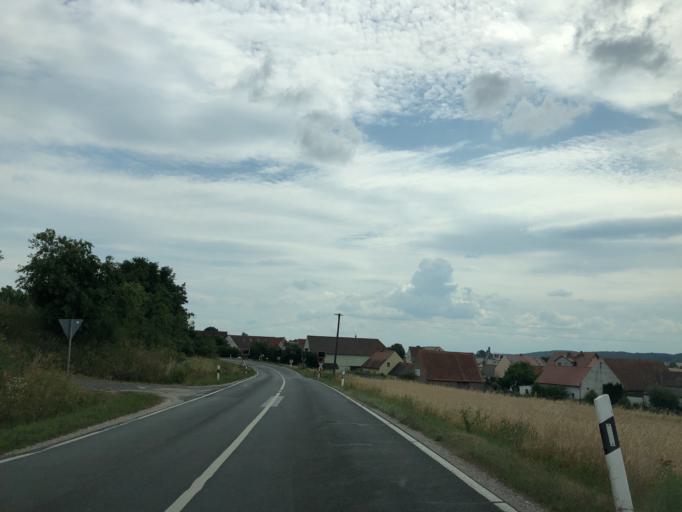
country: DE
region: Bavaria
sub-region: Regierungsbezirk Mittelfranken
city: Wachenroth
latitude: 49.7498
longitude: 10.7013
